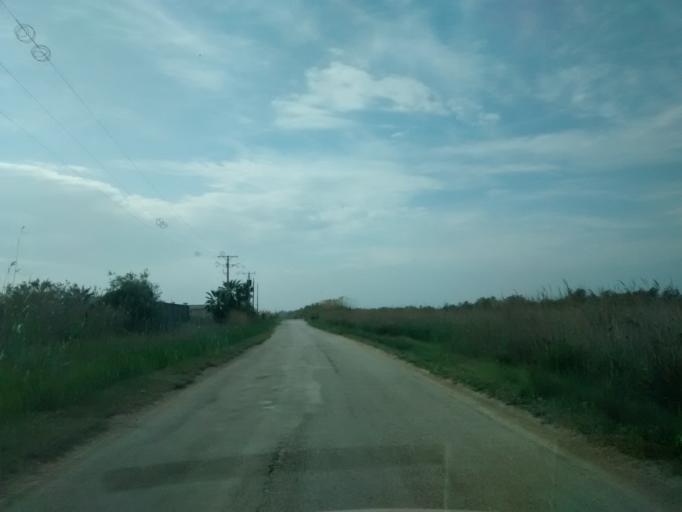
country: ES
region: Catalonia
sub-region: Provincia de Tarragona
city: Deltebre
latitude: 40.6874
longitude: 0.8495
